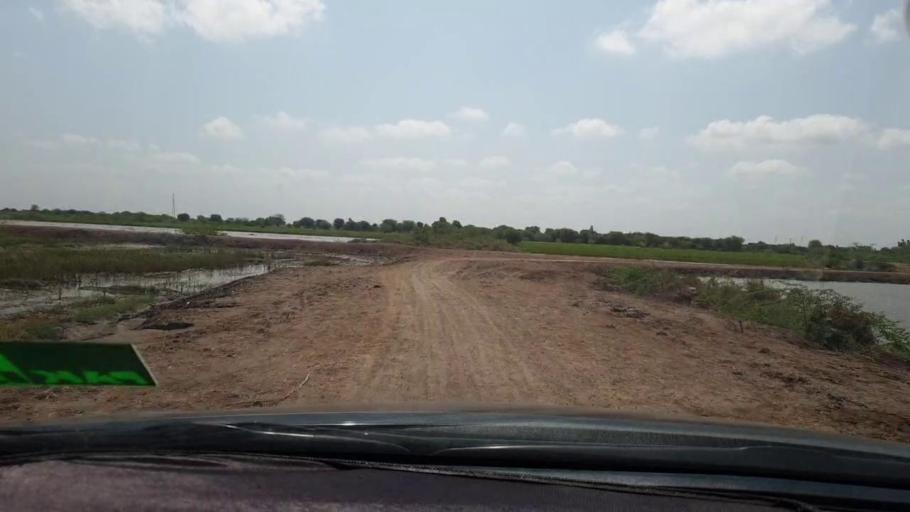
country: PK
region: Sindh
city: Tando Bago
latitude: 24.9344
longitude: 69.0948
